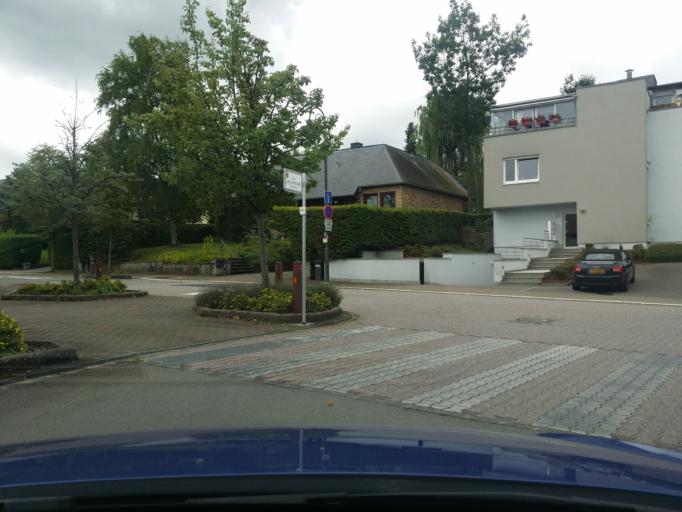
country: LU
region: Luxembourg
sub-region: Canton de Luxembourg
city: Bertrange
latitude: 49.6025
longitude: 6.0506
